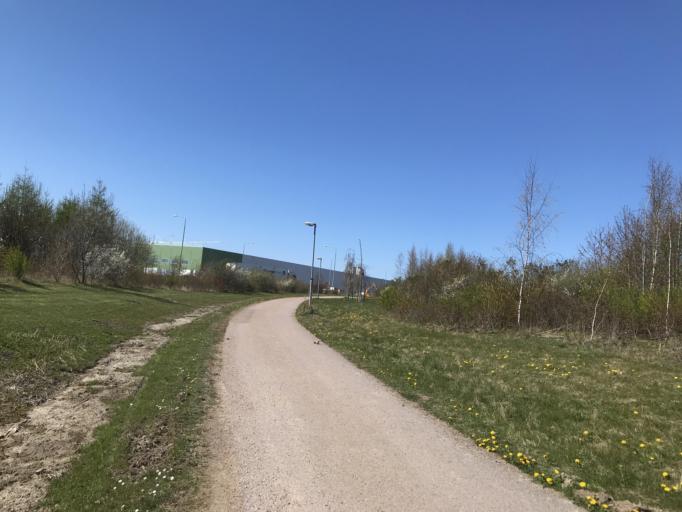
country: SE
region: Skane
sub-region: Landskrona
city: Landskrona
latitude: 55.8748
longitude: 12.8691
